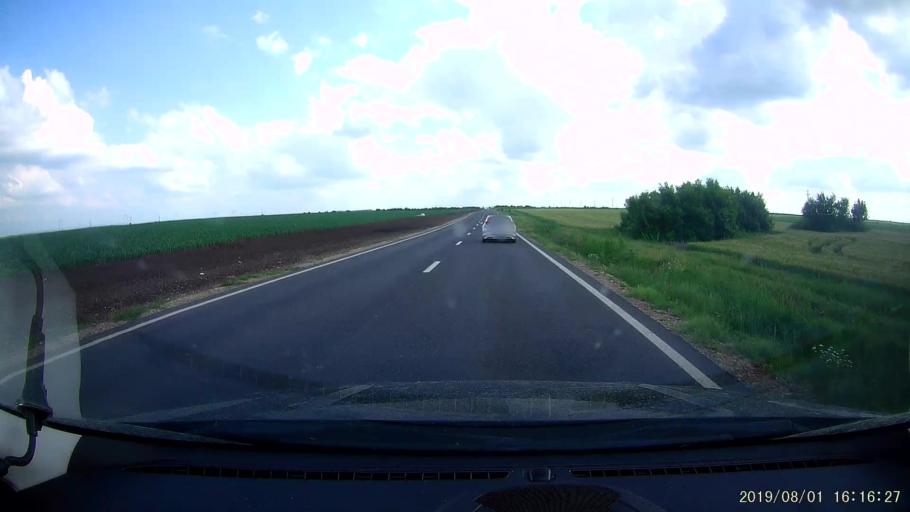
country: RO
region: Calarasi
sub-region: Comuna Stefan Voda
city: Stefan Voda
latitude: 44.3194
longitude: 27.3578
